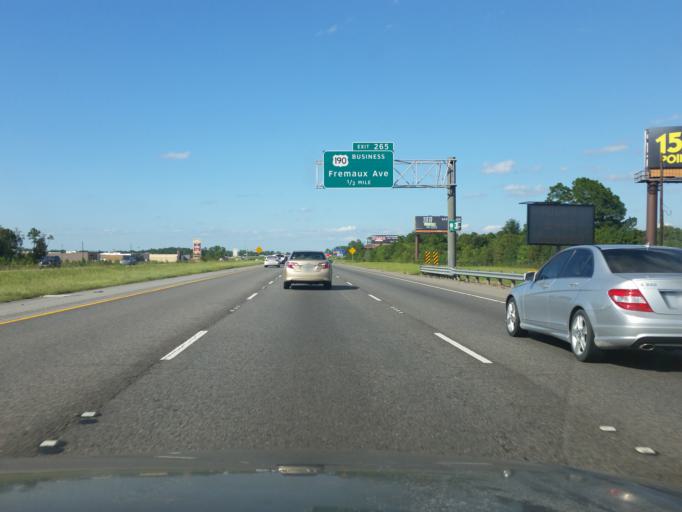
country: US
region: Louisiana
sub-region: Saint Tammany Parish
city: Slidell
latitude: 30.2592
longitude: -89.7590
